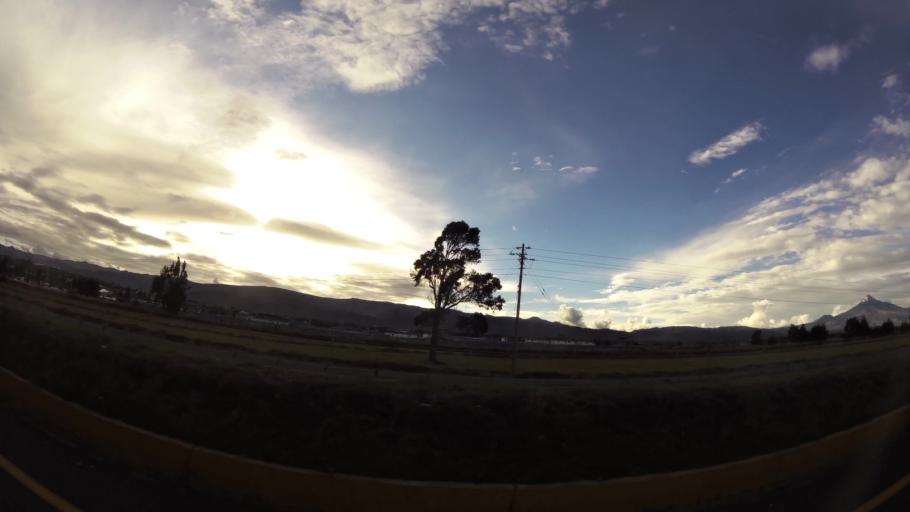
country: EC
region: Cotopaxi
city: Saquisili
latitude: -0.8723
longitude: -78.6272
